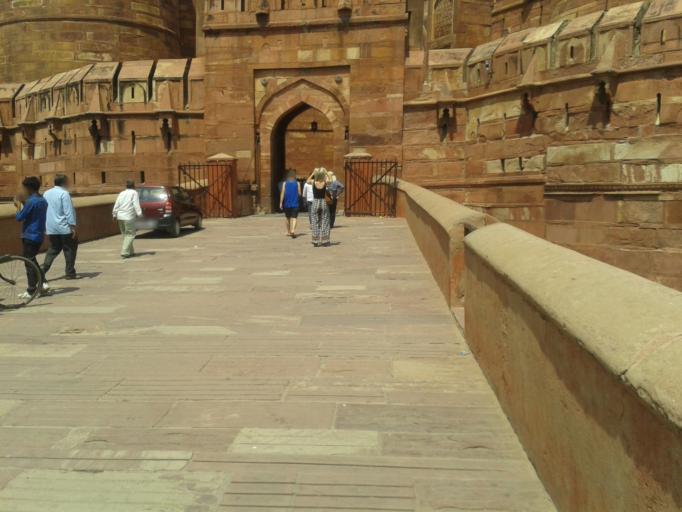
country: IN
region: Uttar Pradesh
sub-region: Agra
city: Agra
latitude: 27.1762
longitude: 78.0219
